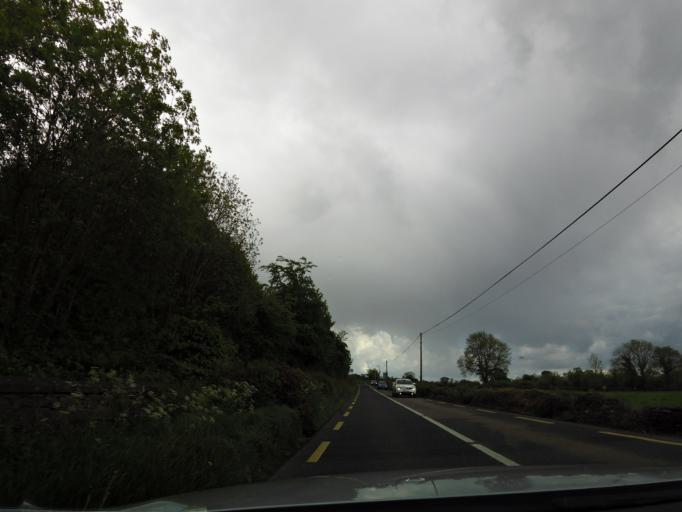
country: IE
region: Munster
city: Thurles
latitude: 52.7063
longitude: -7.8251
